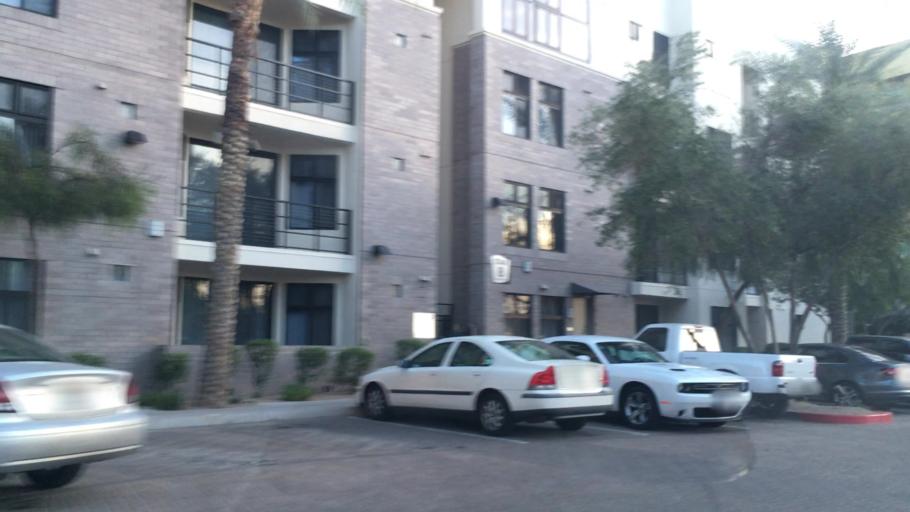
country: US
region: Arizona
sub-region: Maricopa County
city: Tempe
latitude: 33.4340
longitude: -111.9239
